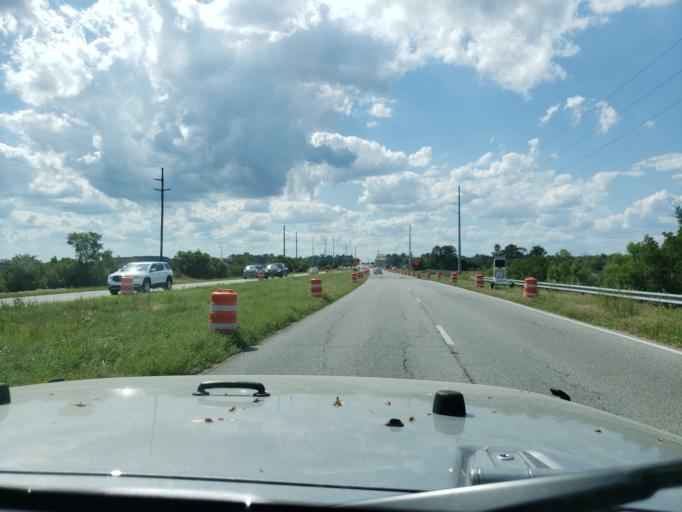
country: US
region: Georgia
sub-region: Chatham County
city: Whitemarsh Island
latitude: 32.0576
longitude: -81.0204
